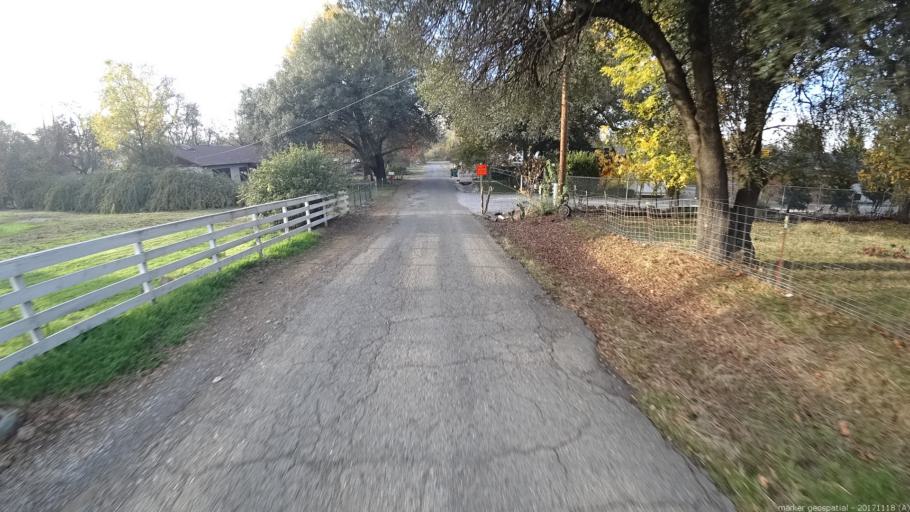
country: US
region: California
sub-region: Shasta County
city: Anderson
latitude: 40.4640
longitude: -122.3260
